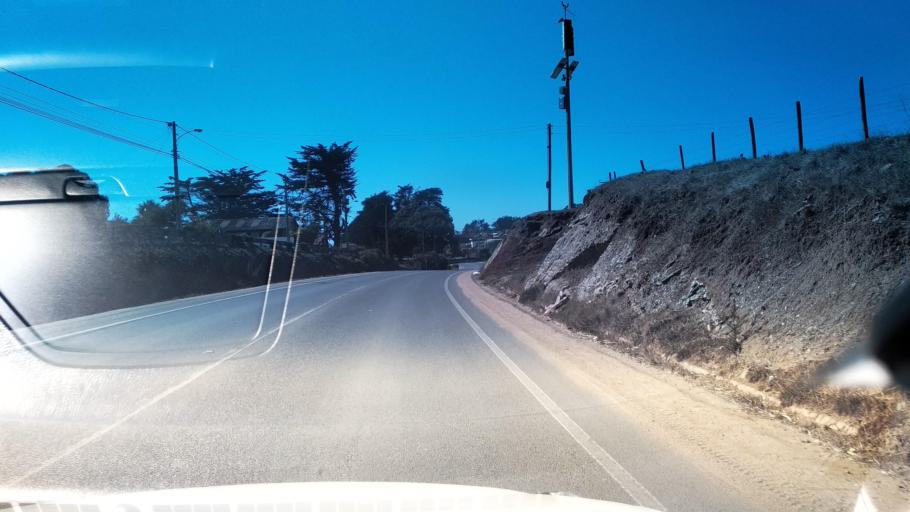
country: CL
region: O'Higgins
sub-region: Provincia de Colchagua
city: Santa Cruz
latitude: -34.4167
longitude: -72.0296
